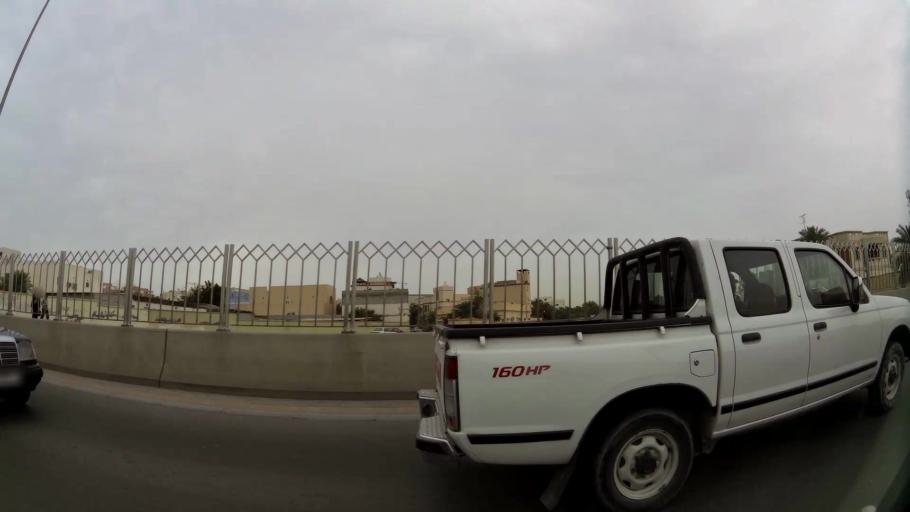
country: BH
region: Manama
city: Jidd Hafs
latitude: 26.2149
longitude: 50.5339
